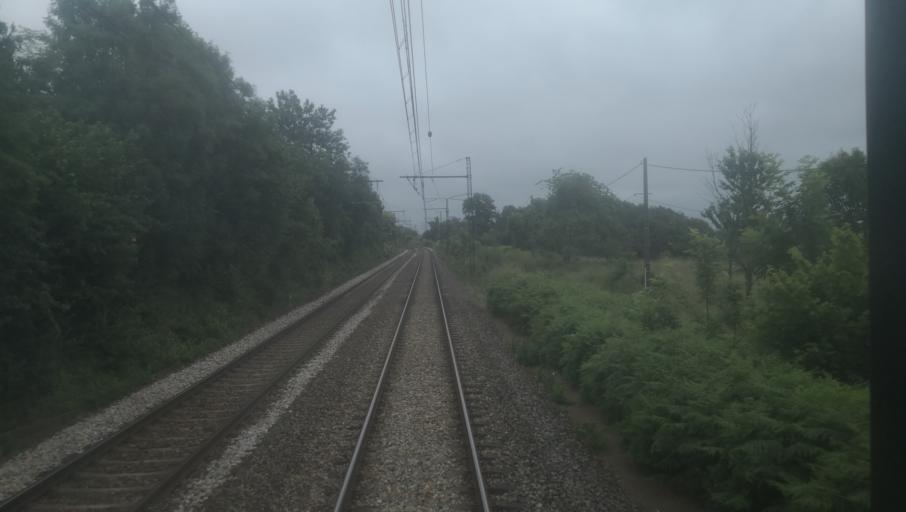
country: FR
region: Limousin
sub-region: Departement de la Creuse
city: Saint-Agnant-de-Versillat
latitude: 46.2848
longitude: 1.4788
